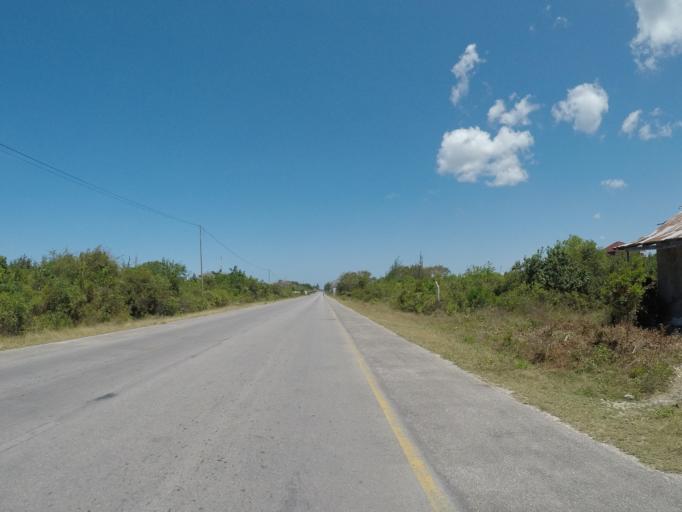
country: TZ
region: Zanzibar Central/South
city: Nganane
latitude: -6.2940
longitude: 39.5375
